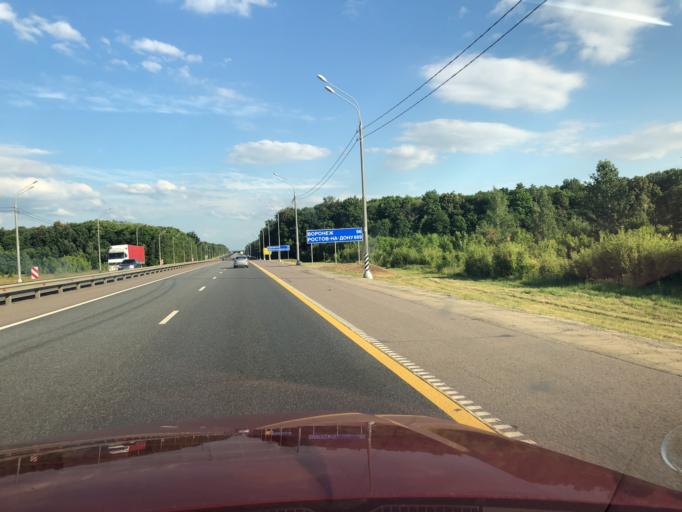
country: RU
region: Lipetsk
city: Zadonsk
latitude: 52.4225
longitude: 38.8339
